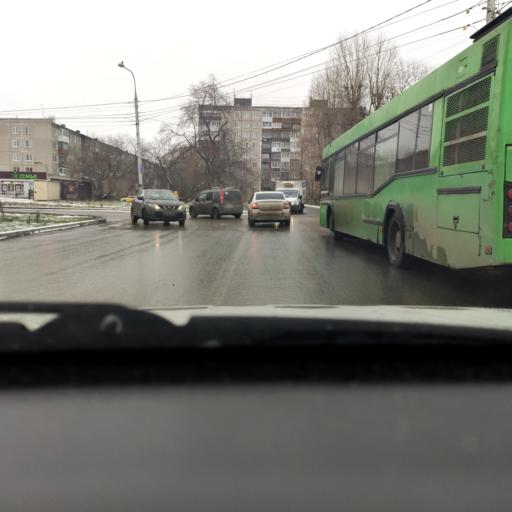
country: RU
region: Perm
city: Perm
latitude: 57.9643
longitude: 56.2240
